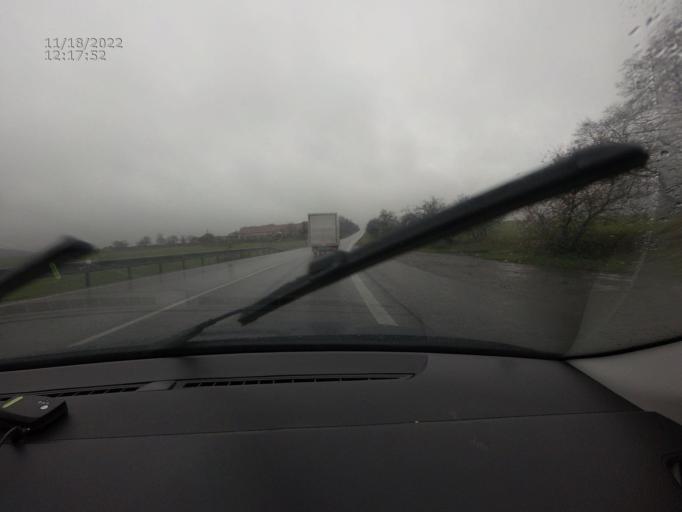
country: CZ
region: Plzensky
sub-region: Okres Plzen-Jih
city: Nepomuk
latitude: 49.4906
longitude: 13.5693
